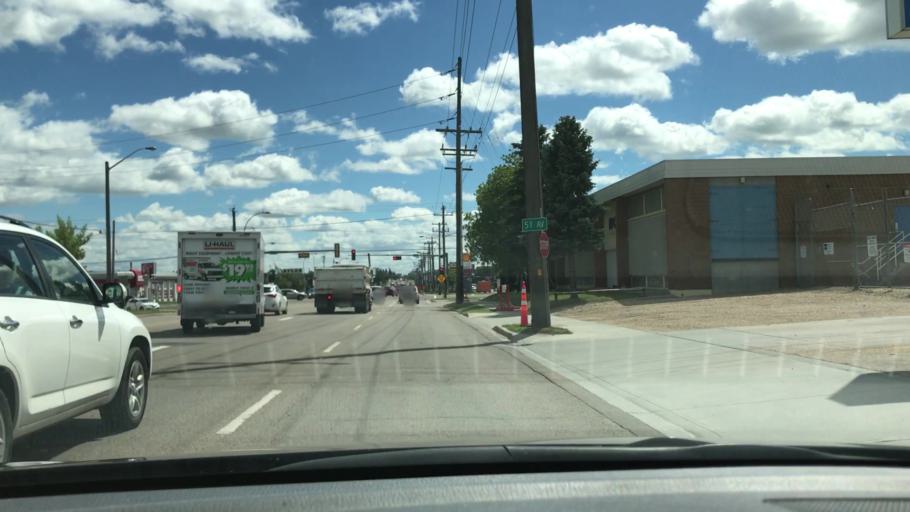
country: CA
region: Alberta
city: Edmonton
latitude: 53.4892
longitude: -113.4862
